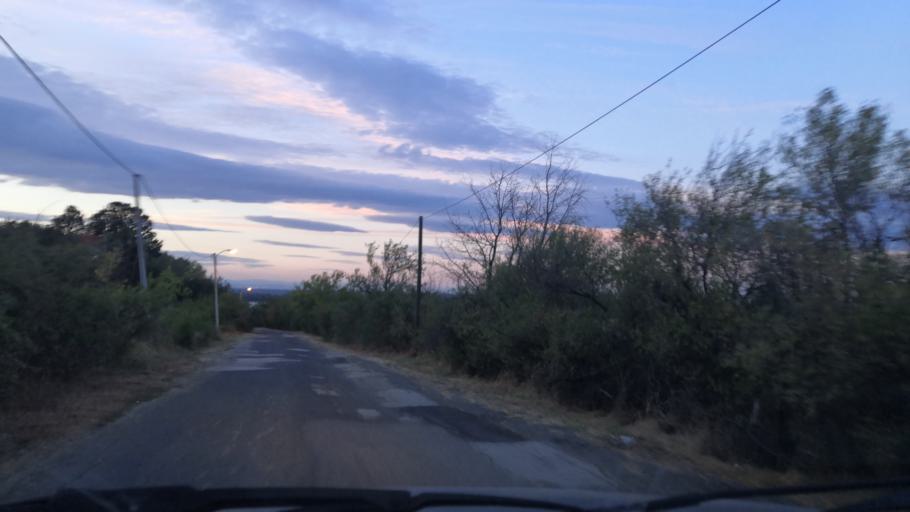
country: RO
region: Mehedinti
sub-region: Comuna Gogosu
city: Balta Verde
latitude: 44.3068
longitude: 22.5493
